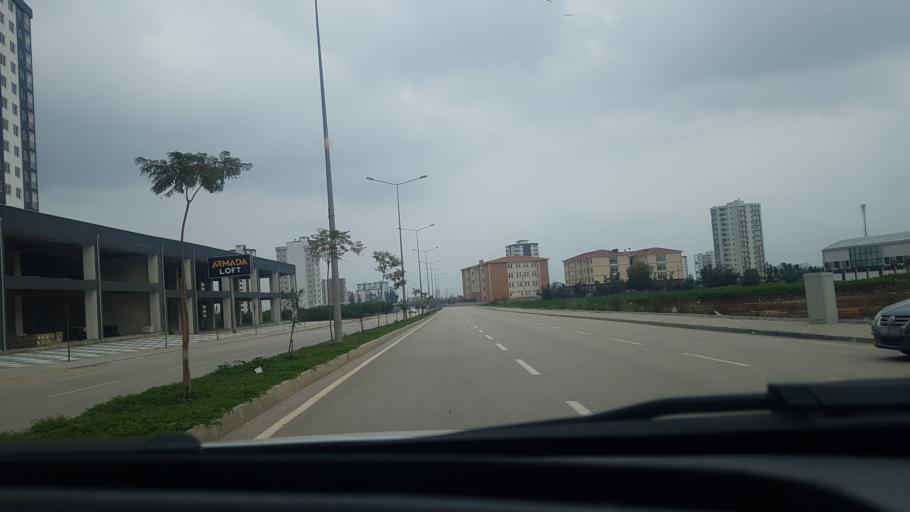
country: TR
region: Adana
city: Seyhan
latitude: 37.0142
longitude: 35.2573
